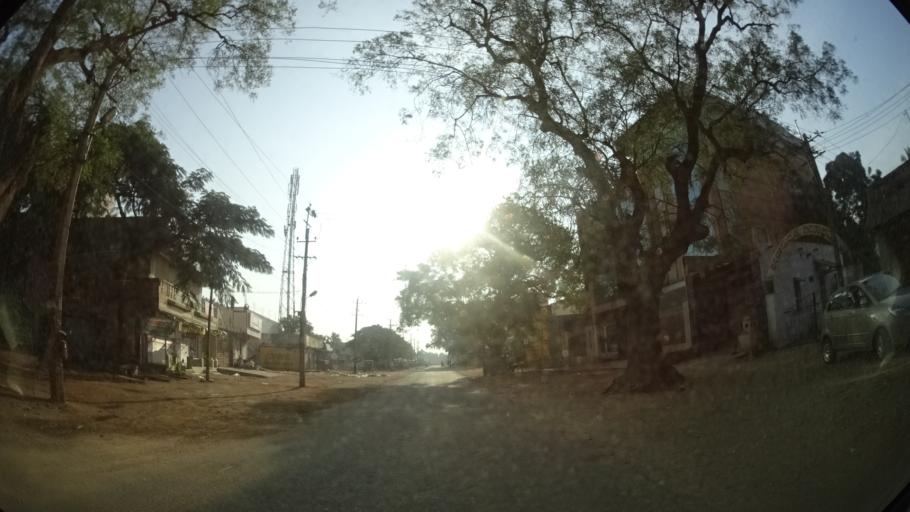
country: IN
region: Karnataka
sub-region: Bellary
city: Hospet
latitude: 15.2657
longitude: 76.4008
